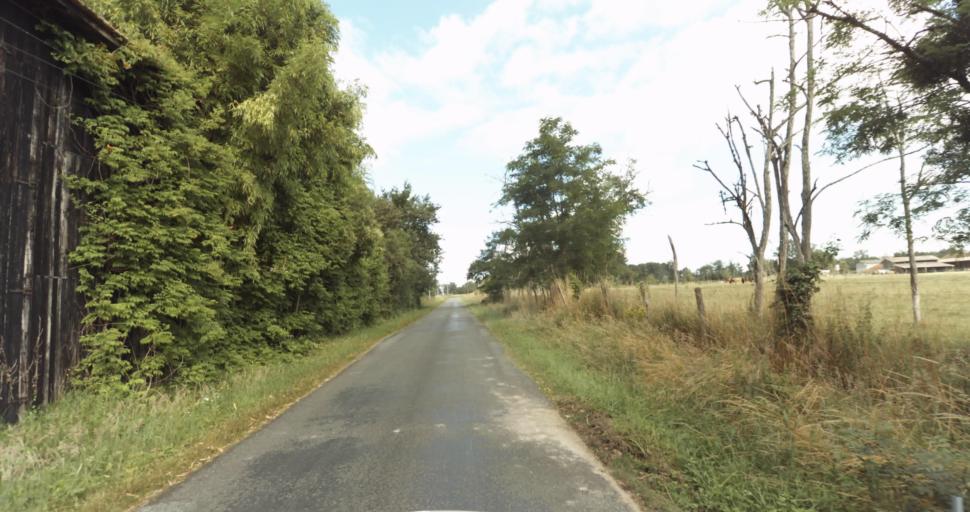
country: FR
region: Aquitaine
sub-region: Departement de la Gironde
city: Bazas
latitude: 44.4553
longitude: -0.1914
